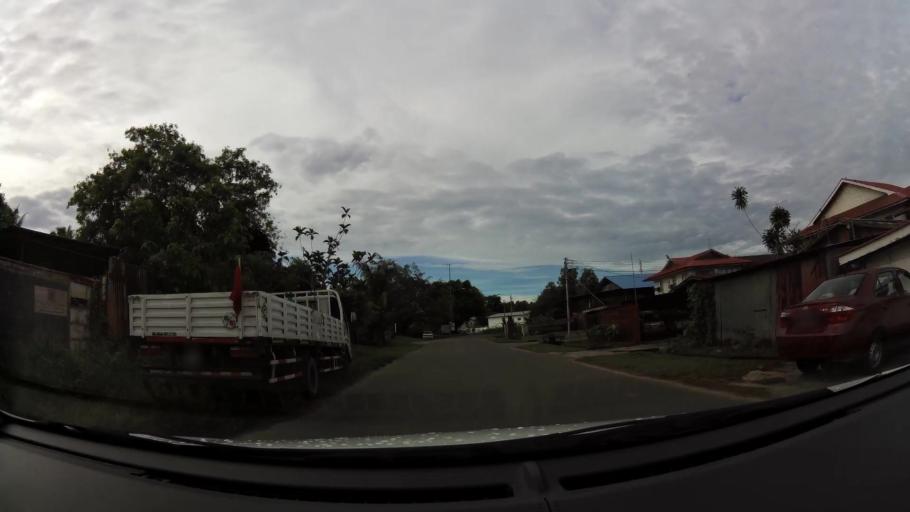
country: BN
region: Belait
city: Seria
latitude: 4.6156
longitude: 114.3504
